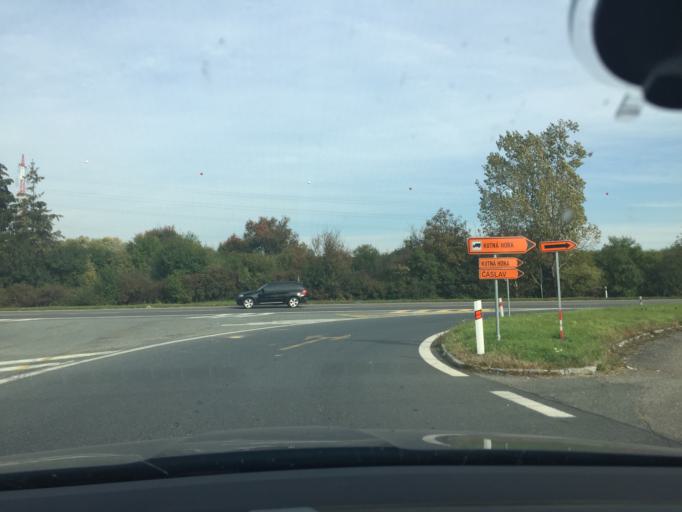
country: CZ
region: Central Bohemia
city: Cirkvice
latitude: 49.9669
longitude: 15.3122
